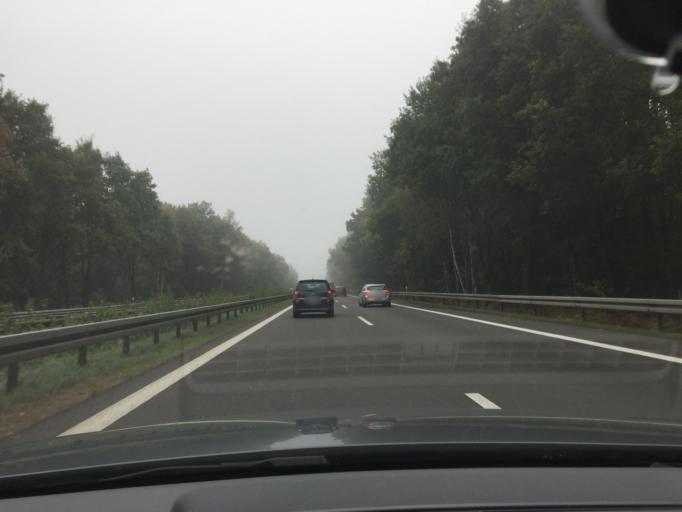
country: DE
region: Brandenburg
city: Bronkow
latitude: 51.6900
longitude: 13.9013
